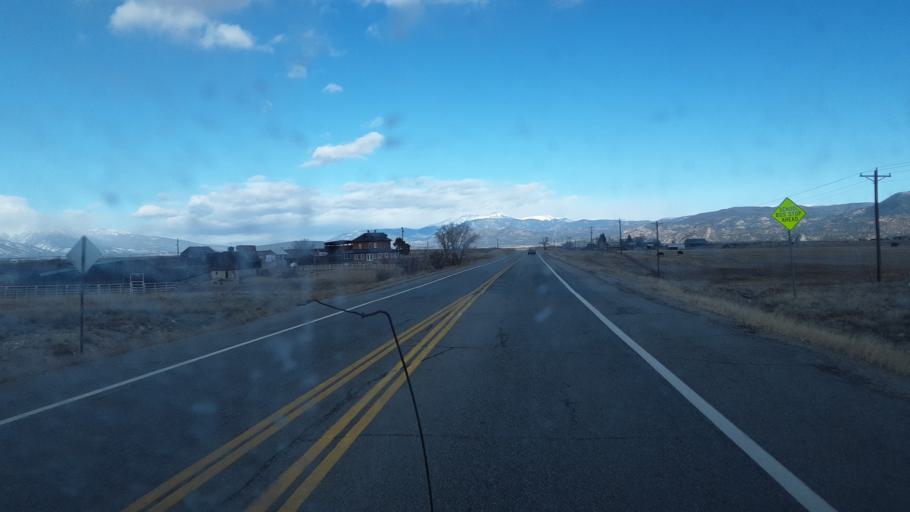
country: US
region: Colorado
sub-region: Chaffee County
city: Buena Vista
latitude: 38.6952
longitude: -106.0901
